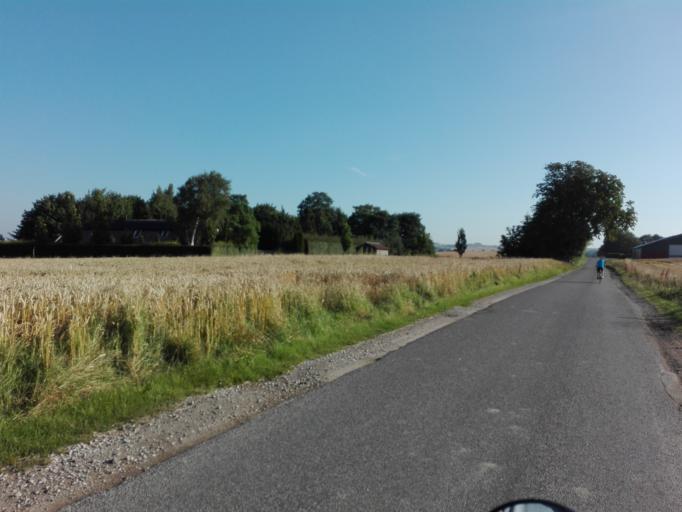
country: DK
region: Central Jutland
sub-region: Arhus Kommune
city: Marslet
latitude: 56.0607
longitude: 10.1468
